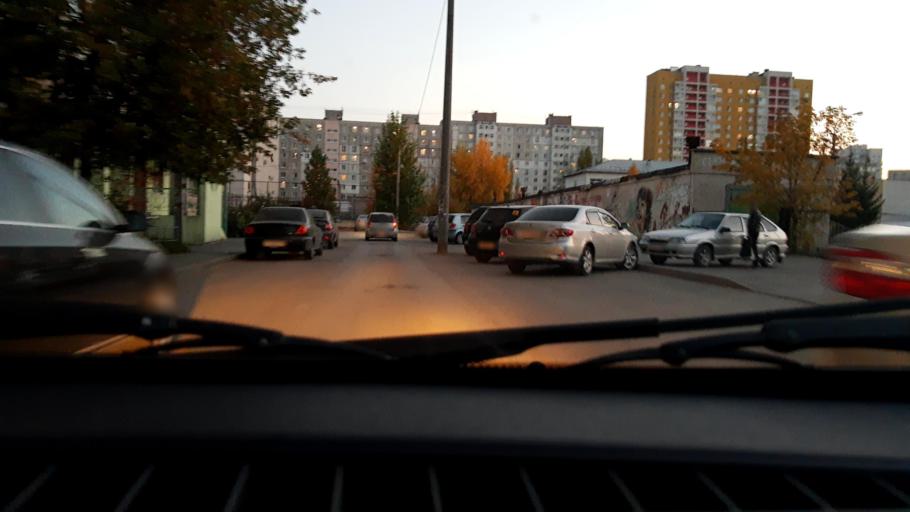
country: RU
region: Bashkortostan
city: Ufa
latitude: 54.7727
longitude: 56.0737
